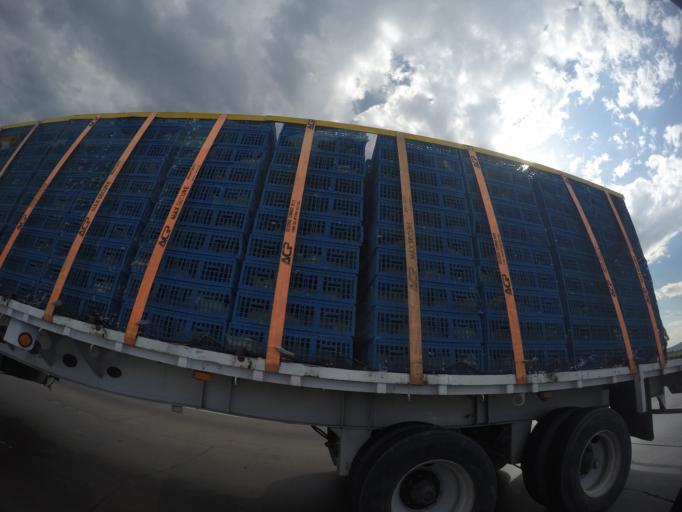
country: MX
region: Queretaro
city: La Estancia
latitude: 20.4485
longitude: -100.0806
